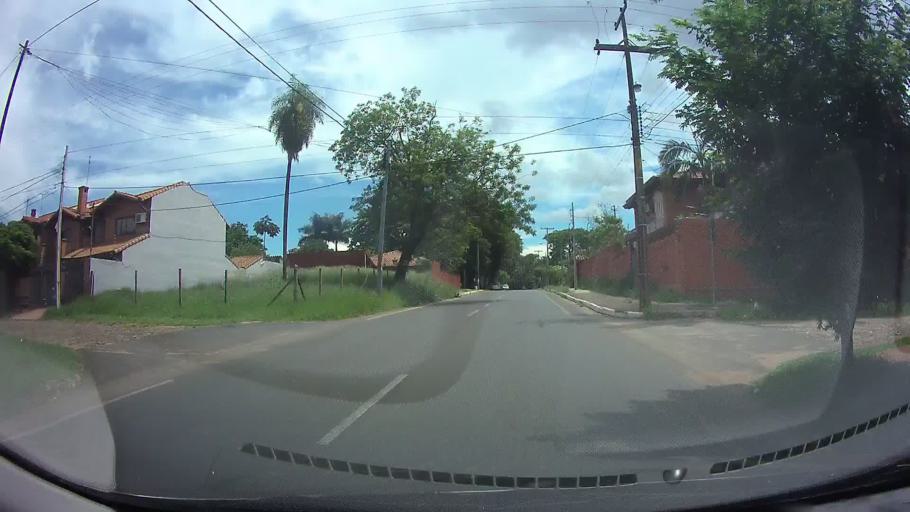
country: PY
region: Central
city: Fernando de la Mora
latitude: -25.3194
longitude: -57.5292
